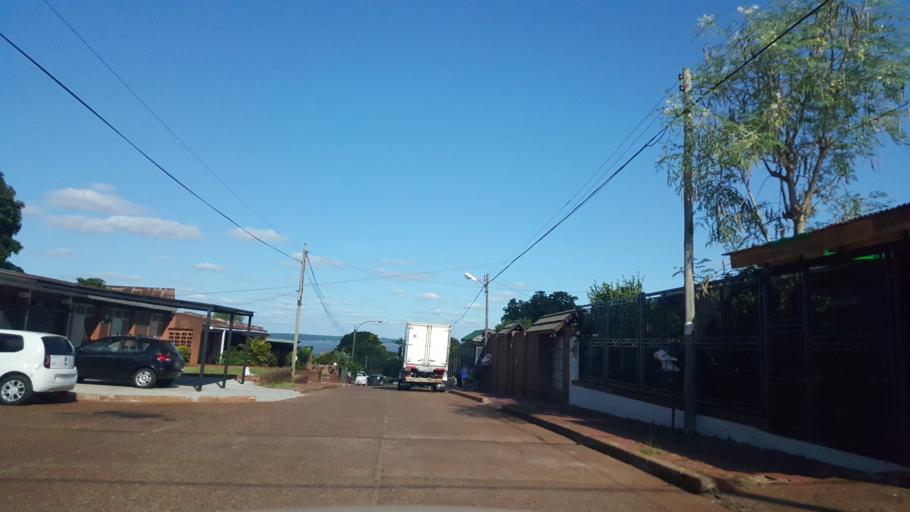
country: AR
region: Misiones
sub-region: Departamento de Capital
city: Posadas
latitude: -27.3923
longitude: -55.8953
